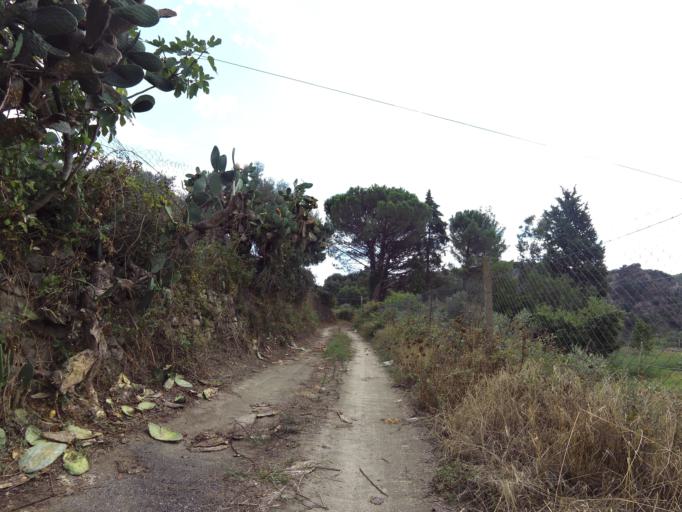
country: IT
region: Calabria
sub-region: Provincia di Reggio Calabria
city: Stilo
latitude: 38.4536
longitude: 16.4712
